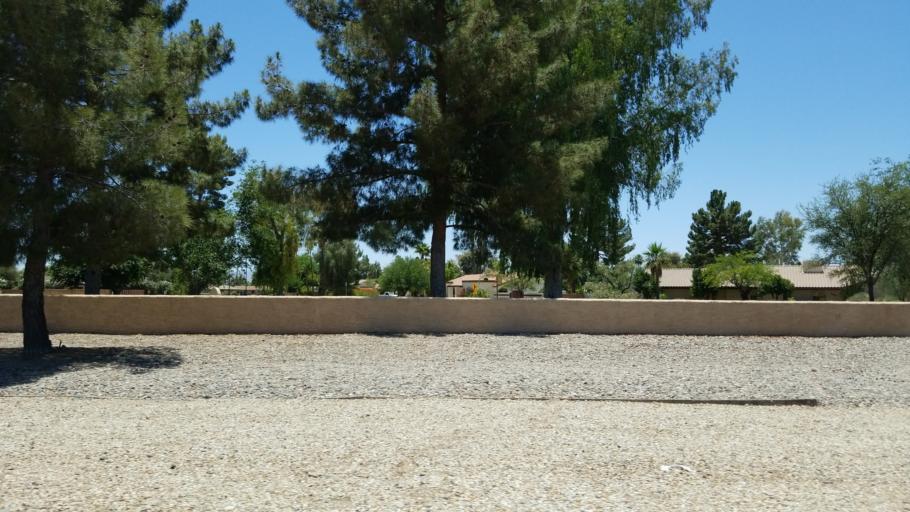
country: US
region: Arizona
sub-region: Maricopa County
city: Litchfield Park
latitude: 33.5078
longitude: -112.3430
